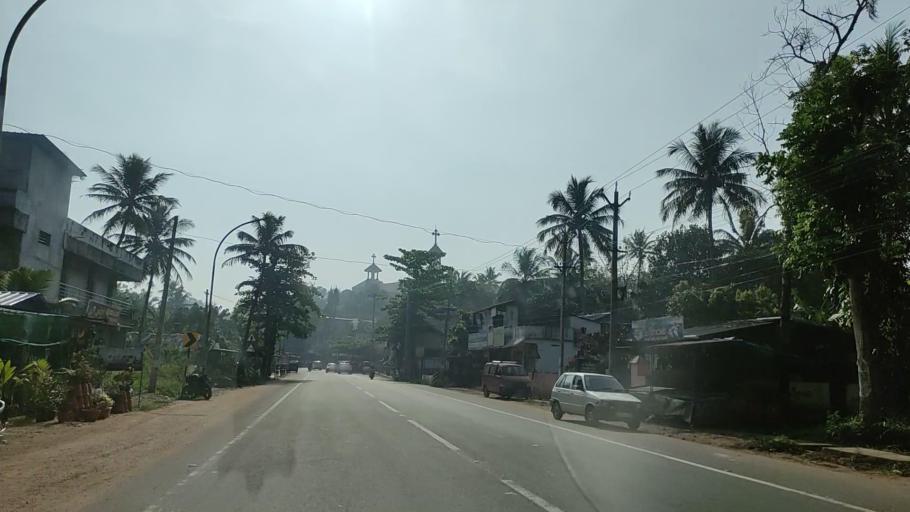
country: IN
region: Kerala
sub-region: Kollam
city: Punalur
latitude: 8.9734
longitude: 76.8224
